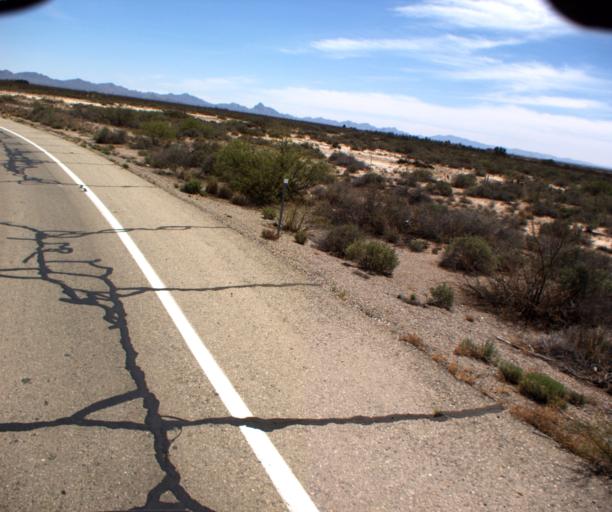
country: US
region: New Mexico
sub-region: Hidalgo County
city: Lordsburg
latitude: 32.2561
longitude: -109.1938
